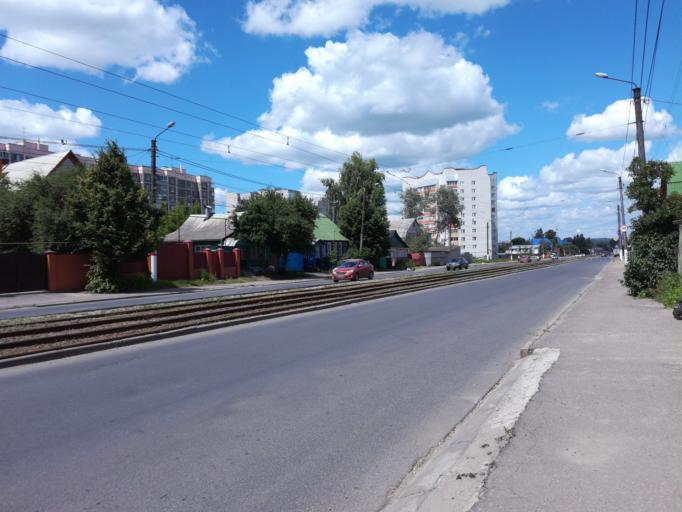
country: RU
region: Kursk
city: Kursk
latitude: 51.7493
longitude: 36.2460
